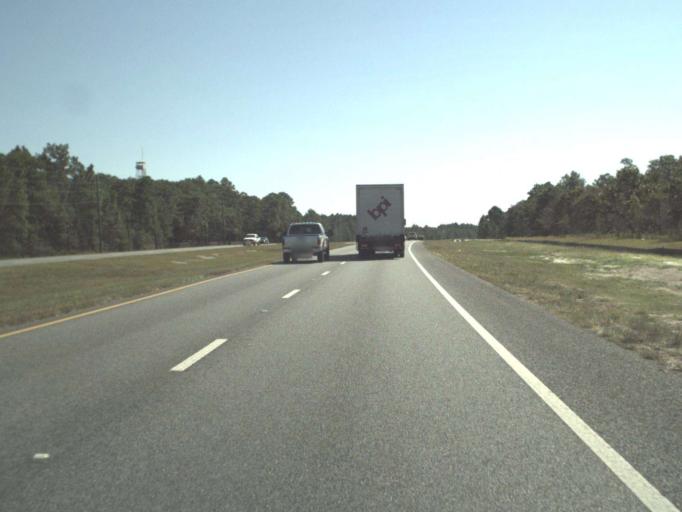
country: US
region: Florida
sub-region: Walton County
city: Seaside
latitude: 30.3536
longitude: -86.0895
